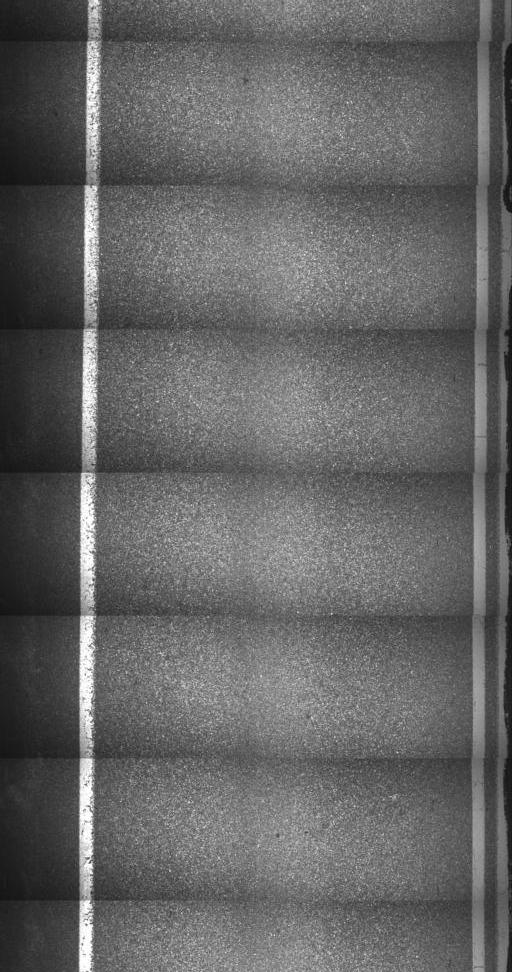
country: US
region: Vermont
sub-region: Washington County
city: Northfield
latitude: 44.1017
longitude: -72.8606
